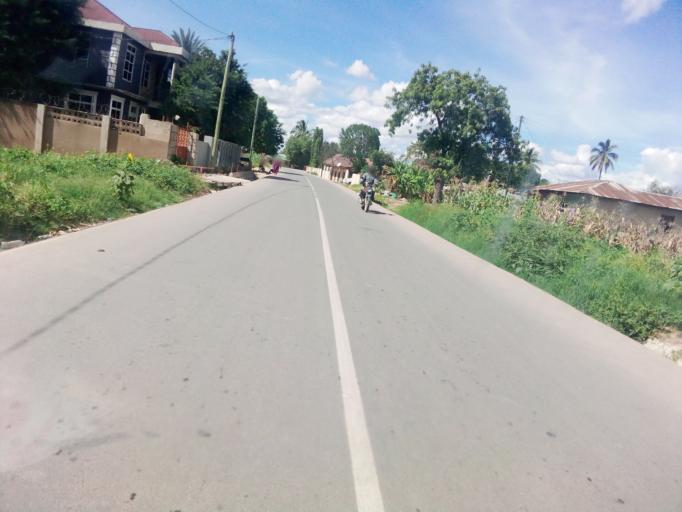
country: TZ
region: Dodoma
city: Dodoma
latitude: -6.1728
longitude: 35.7591
